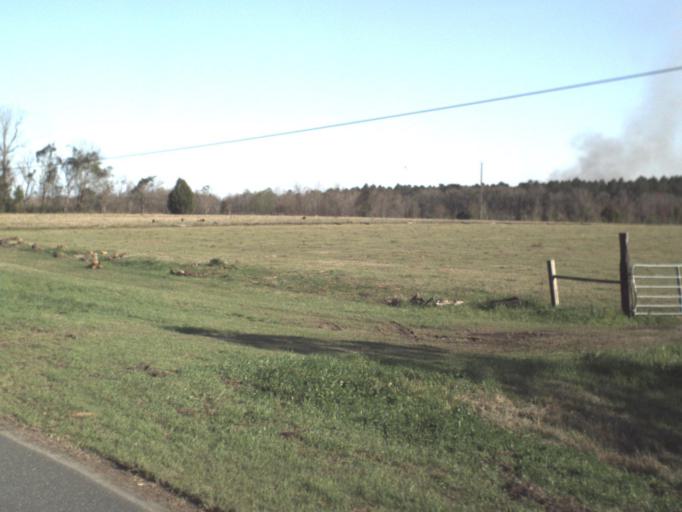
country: US
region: Florida
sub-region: Jackson County
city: Sneads
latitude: 30.7197
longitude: -85.0597
